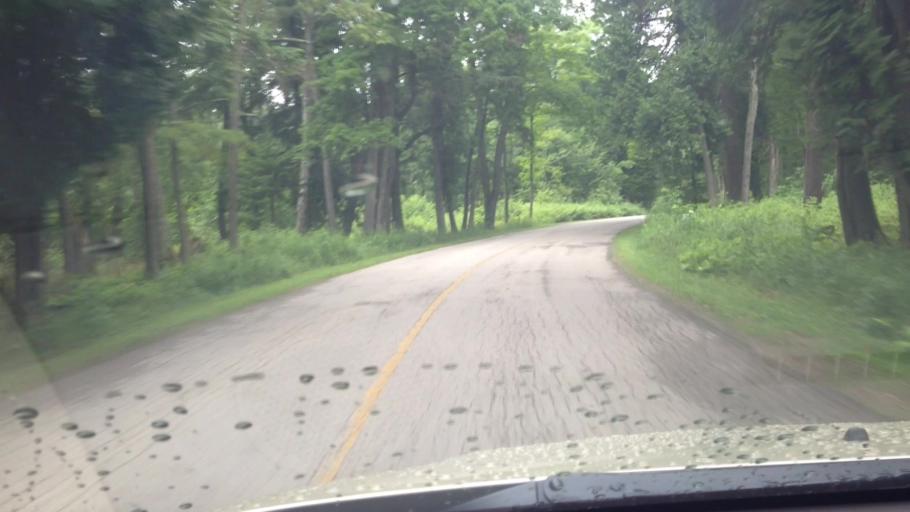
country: US
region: Michigan
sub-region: Menominee County
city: Menominee
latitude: 45.3929
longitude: -87.3656
